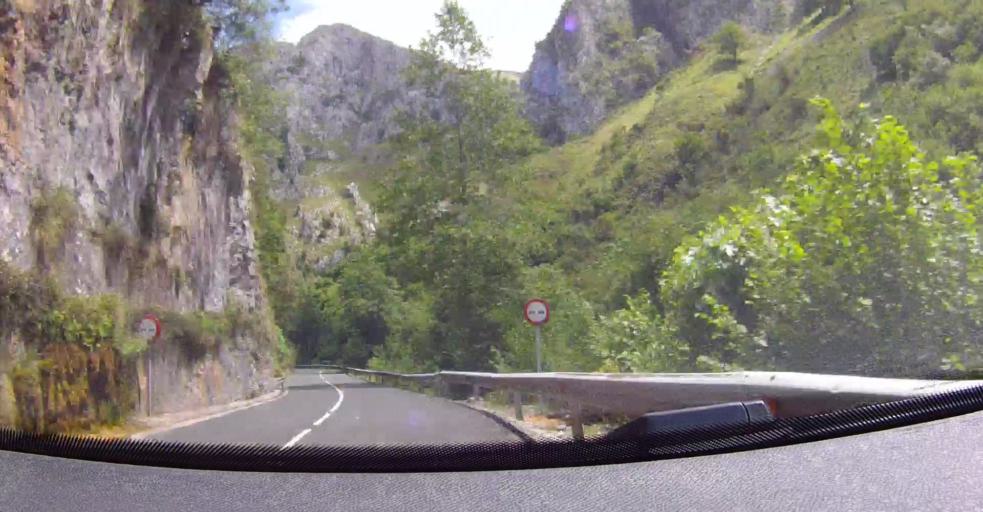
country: ES
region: Cantabria
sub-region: Provincia de Cantabria
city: Tresviso
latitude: 43.2946
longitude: -4.6106
